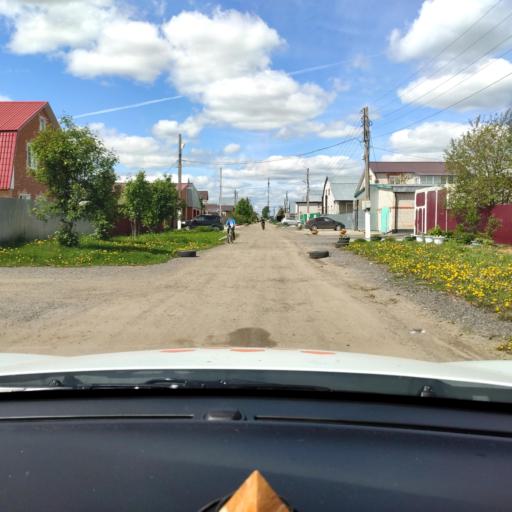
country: RU
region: Tatarstan
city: Osinovo
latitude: 55.8799
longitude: 48.8687
